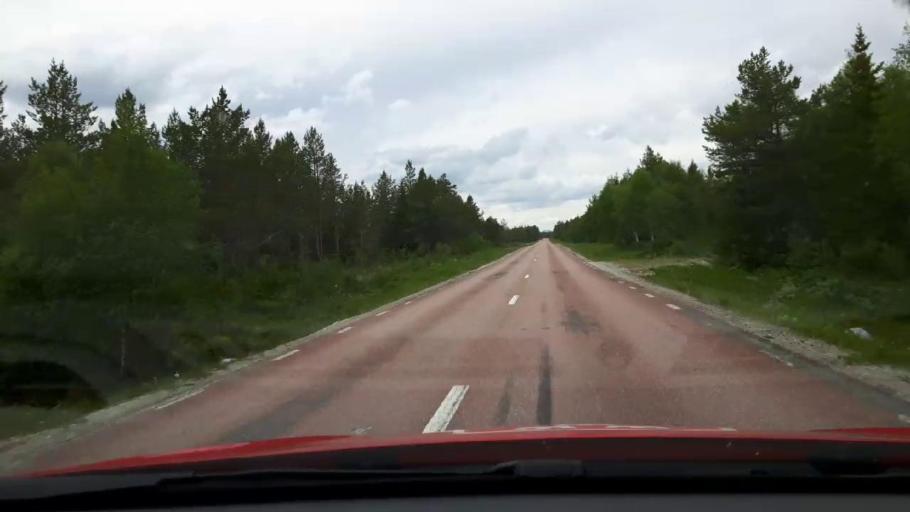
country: NO
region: Hedmark
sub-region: Engerdal
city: Engerdal
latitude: 62.4813
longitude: 12.6626
